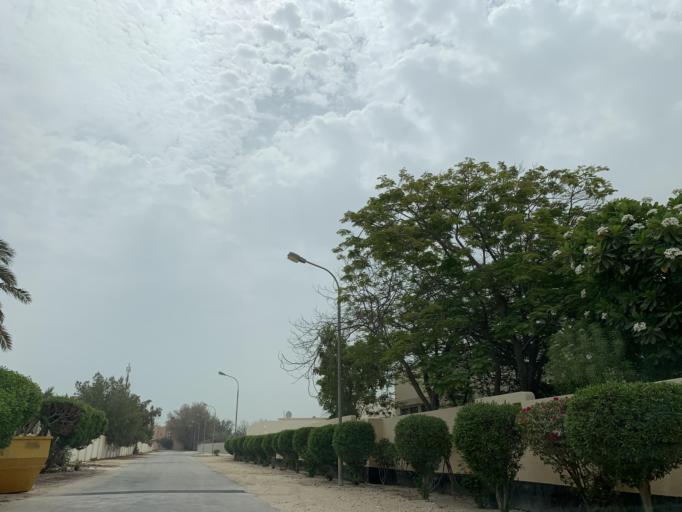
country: BH
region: Central Governorate
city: Madinat Hamad
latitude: 26.1782
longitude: 50.4701
